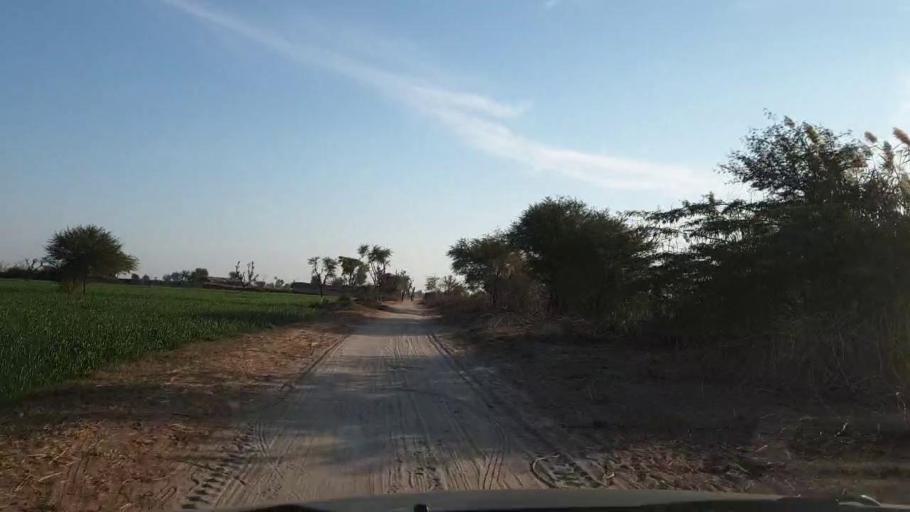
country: PK
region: Sindh
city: Khadro
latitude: 26.2226
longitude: 68.7400
